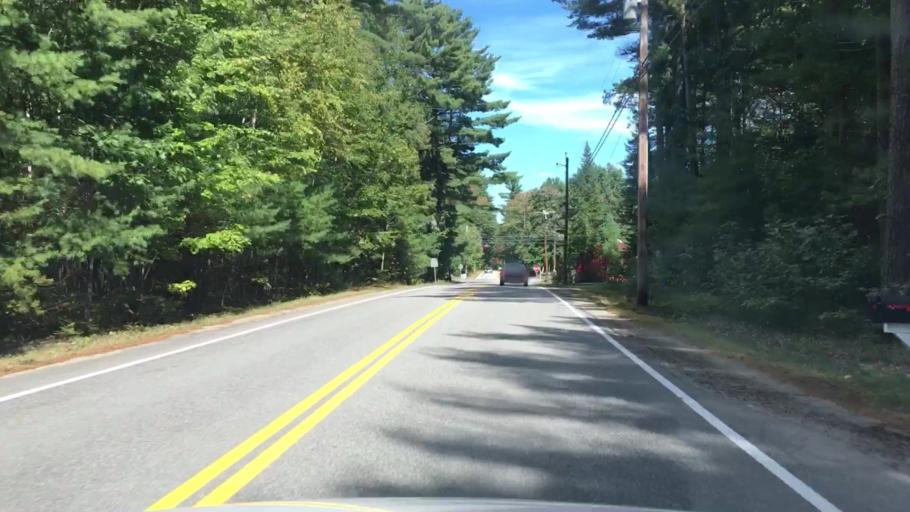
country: US
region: Maine
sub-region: Cumberland County
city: West Scarborough
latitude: 43.5929
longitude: -70.4322
